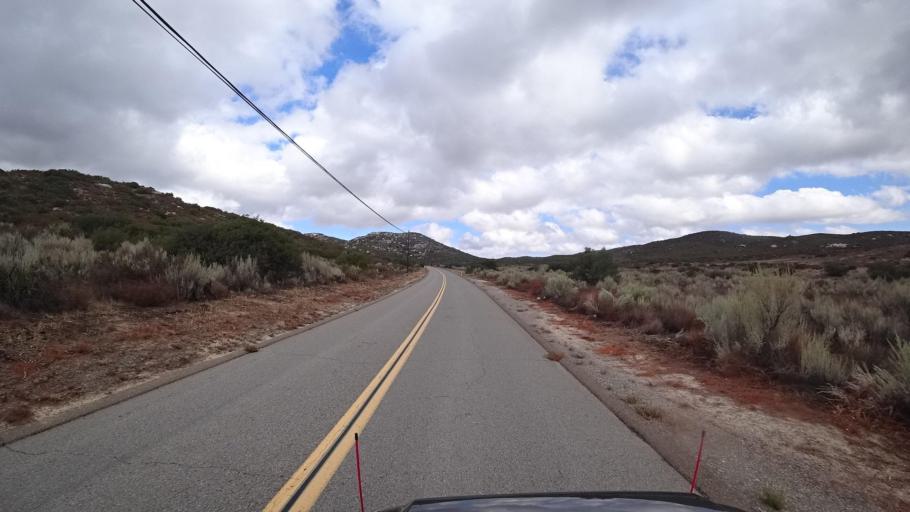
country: US
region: California
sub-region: San Diego County
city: Campo
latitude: 32.6614
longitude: -116.4268
